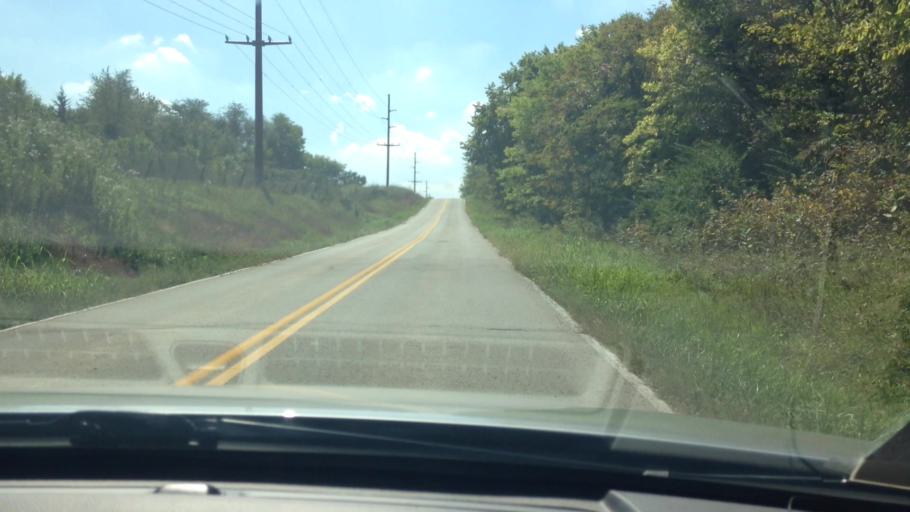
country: US
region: Missouri
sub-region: Platte County
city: Platte City
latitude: 39.3533
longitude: -94.7330
